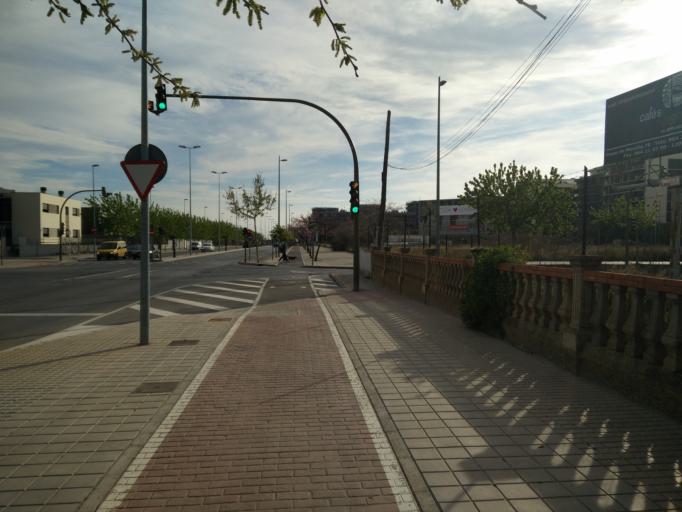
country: ES
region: Valencia
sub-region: Provincia de Castello
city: Castello de la Plana
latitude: 39.9798
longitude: -0.0548
